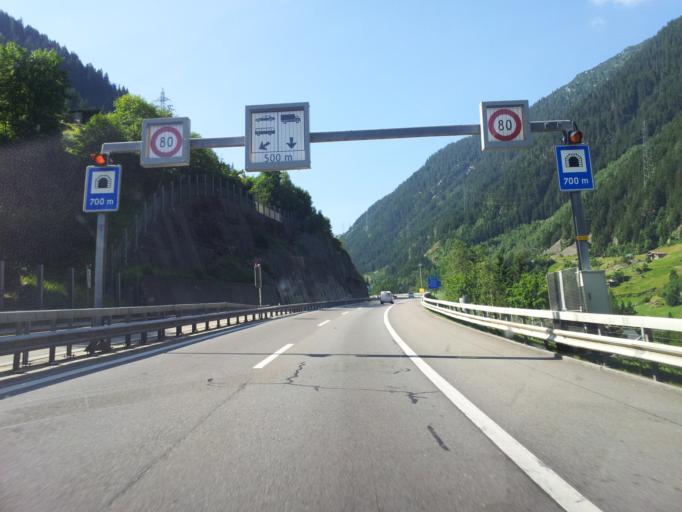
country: CH
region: Uri
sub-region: Uri
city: Andermatt
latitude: 46.6949
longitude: 8.5968
